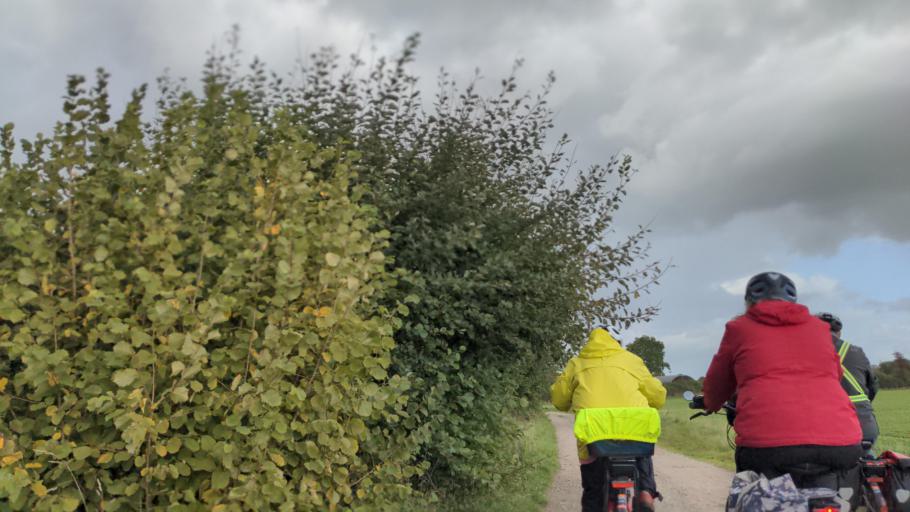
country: DE
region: Schleswig-Holstein
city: Krummesse
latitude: 53.8173
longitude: 10.6313
